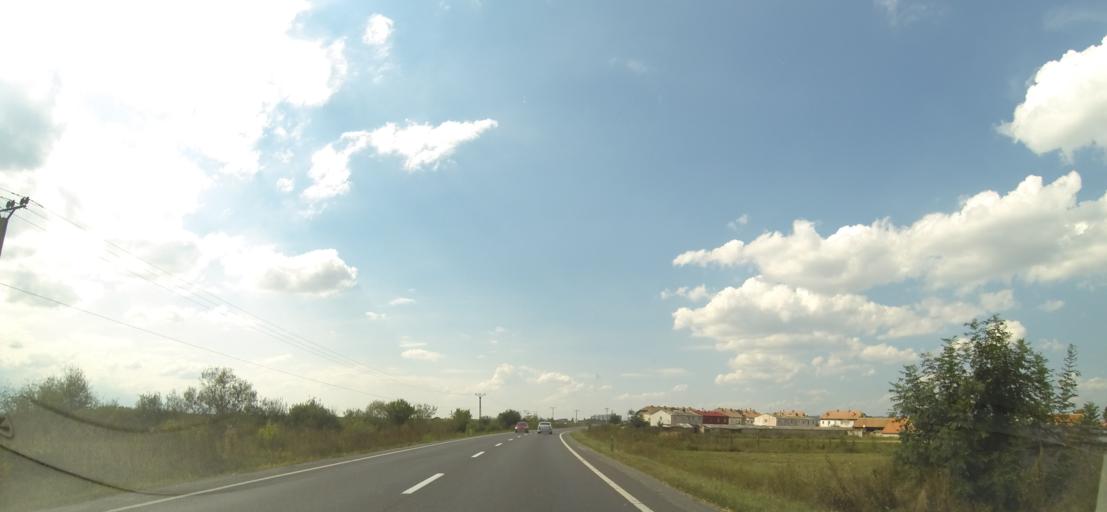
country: RO
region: Brasov
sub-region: Comuna Sercaia
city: Sercaia
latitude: 45.8304
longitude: 25.1306
